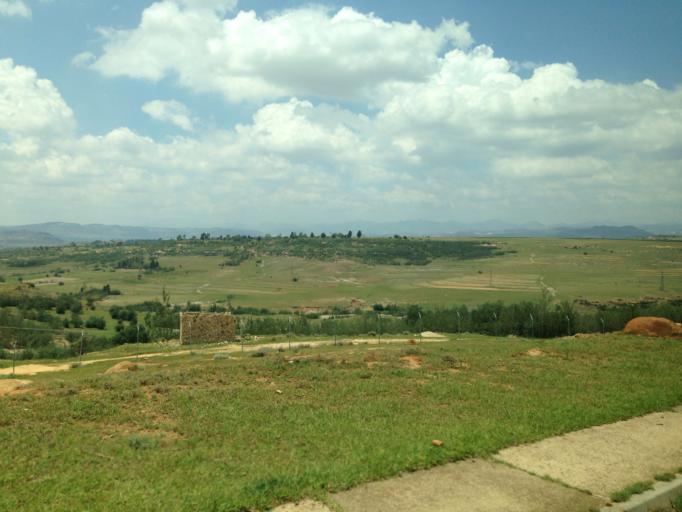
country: LS
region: Maseru
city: Maseru
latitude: -29.4545
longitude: 27.5629
